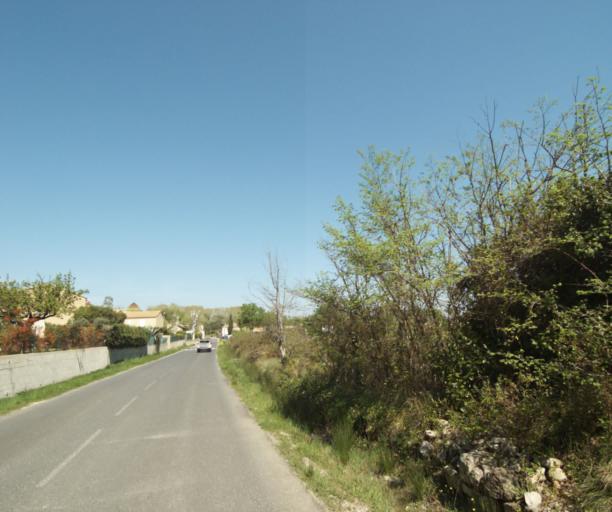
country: FR
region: Languedoc-Roussillon
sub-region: Departement de l'Herault
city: Castries
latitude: 43.6735
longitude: 3.9904
